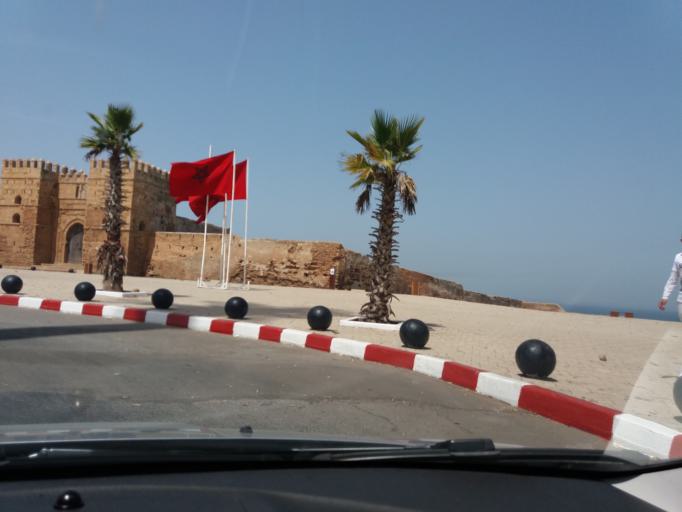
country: MA
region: Gharb-Chrarda-Beni Hssen
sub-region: Kenitra Province
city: Kenitra
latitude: 34.2640
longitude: -6.6557
